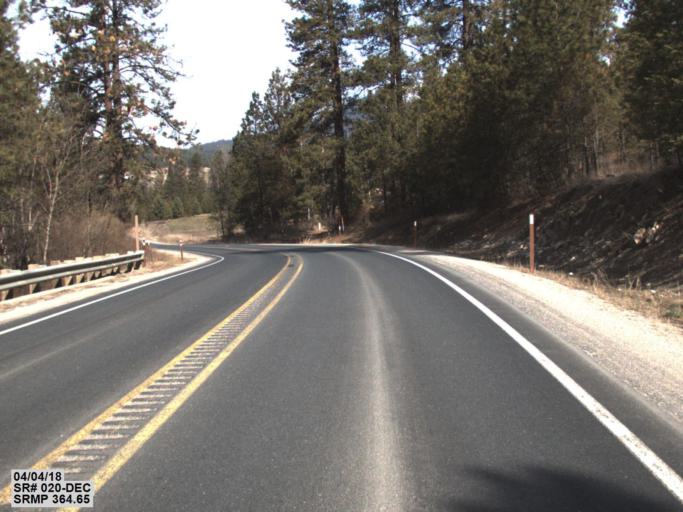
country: US
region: Washington
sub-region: Stevens County
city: Colville
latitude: 48.5067
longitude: -117.7200
